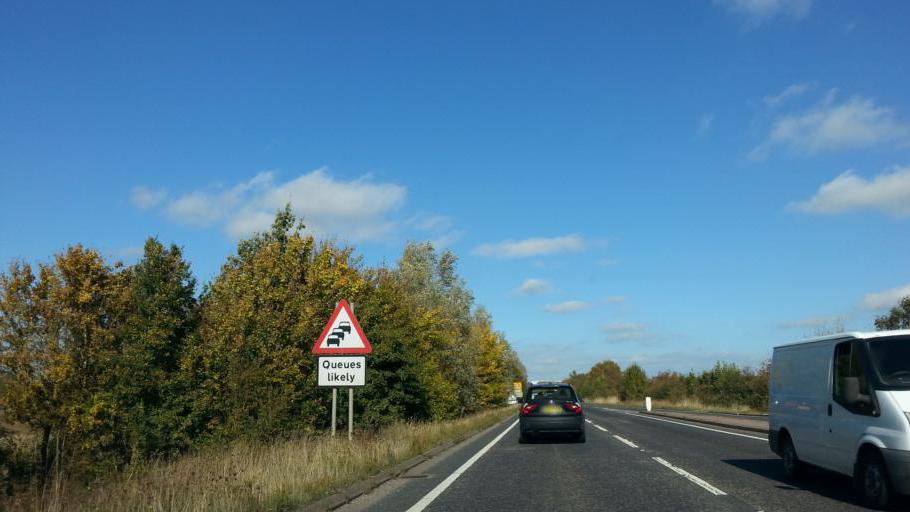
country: GB
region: England
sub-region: Northamptonshire
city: Thrapston
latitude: 52.3833
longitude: -0.5239
